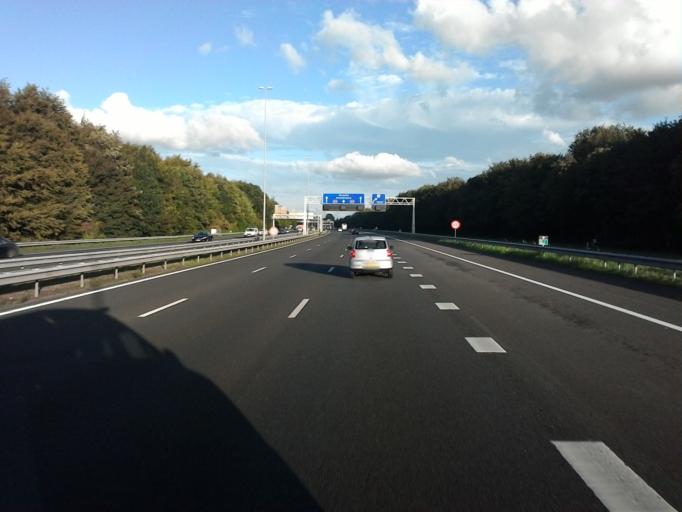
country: NL
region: North Holland
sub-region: Gemeente Amstelveen
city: Amstelveen
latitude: 52.3080
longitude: 4.8257
